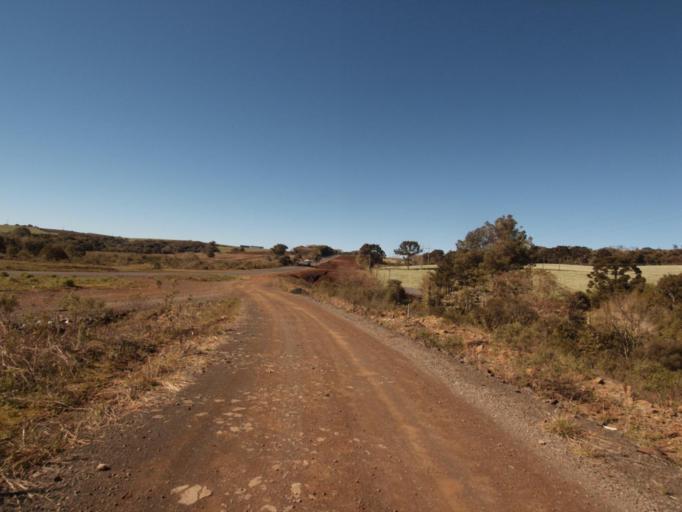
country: BR
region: Santa Catarina
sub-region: Xanxere
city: Xanxere
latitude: -26.8815
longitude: -52.3702
